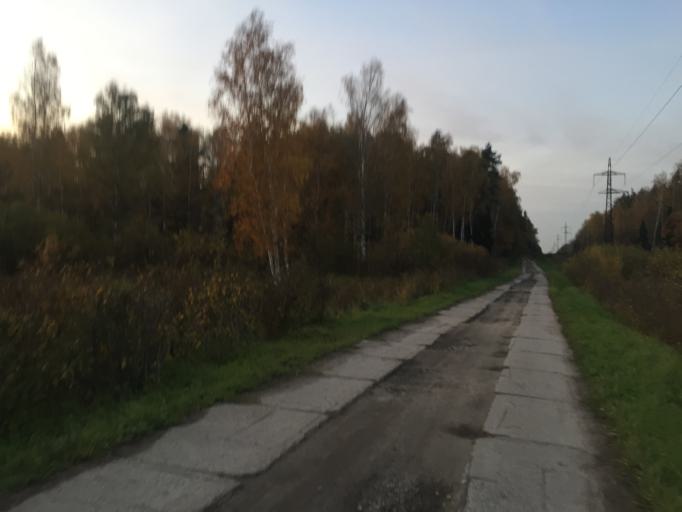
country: RU
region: Moskovskaya
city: Druzhba
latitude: 55.8639
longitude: 37.7680
